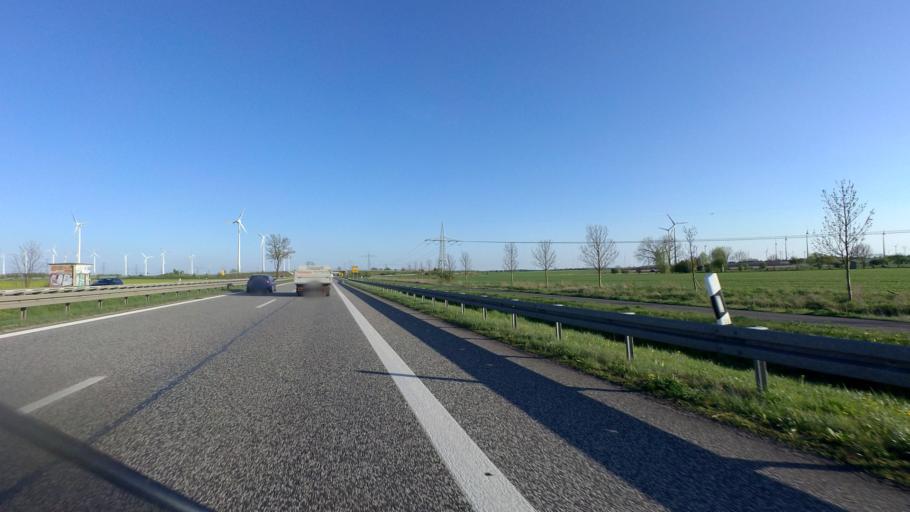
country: DE
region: Brandenburg
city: Nauen
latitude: 52.5815
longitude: 12.9029
